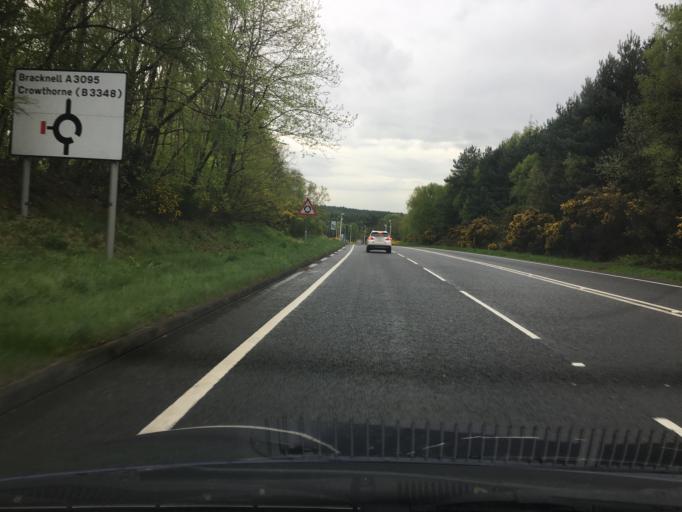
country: GB
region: England
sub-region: Bracknell Forest
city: Crowthorne
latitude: 51.3652
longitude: -0.7673
